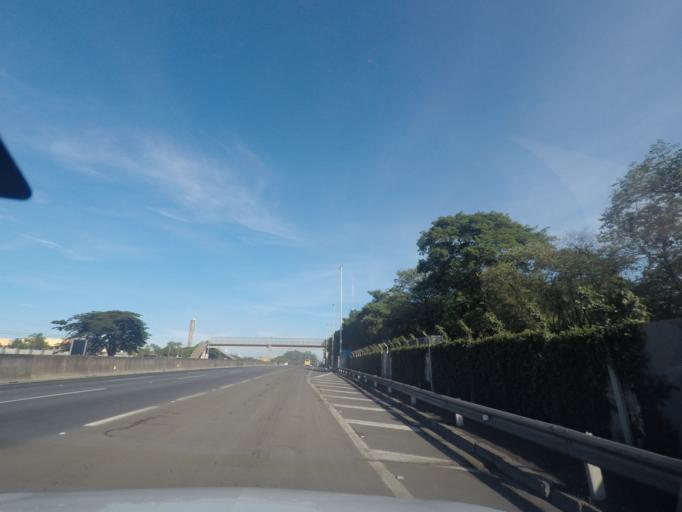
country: BR
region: Sao Paulo
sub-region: Nova Odessa
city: Nova Odessa
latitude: -22.7350
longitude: -47.2838
